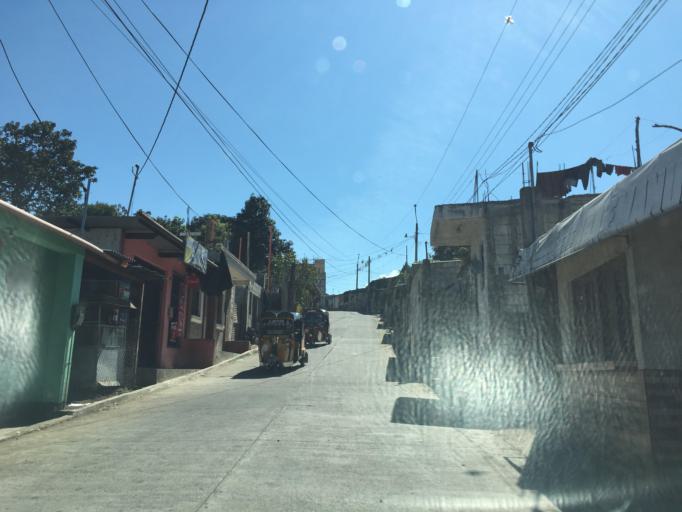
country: GT
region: Solola
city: San Antonio Palopo
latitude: 14.6628
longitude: -91.1632
